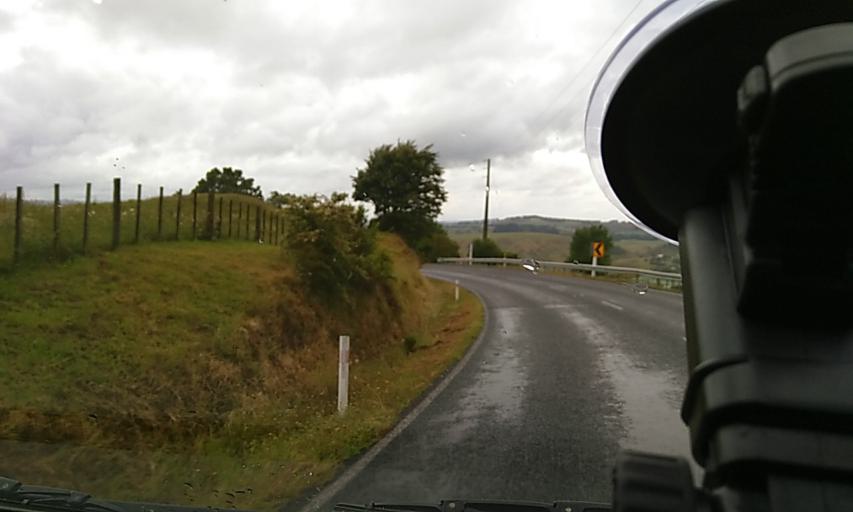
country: NZ
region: Auckland
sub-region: Auckland
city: Pukekohe East
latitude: -37.3192
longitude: 174.9358
